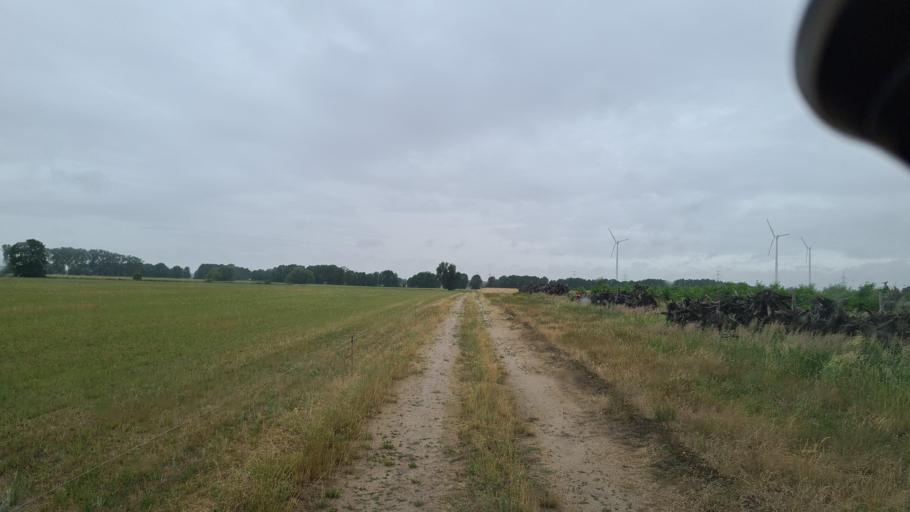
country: DE
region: Saxony-Anhalt
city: Holzdorf
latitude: 51.8193
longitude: 13.1573
